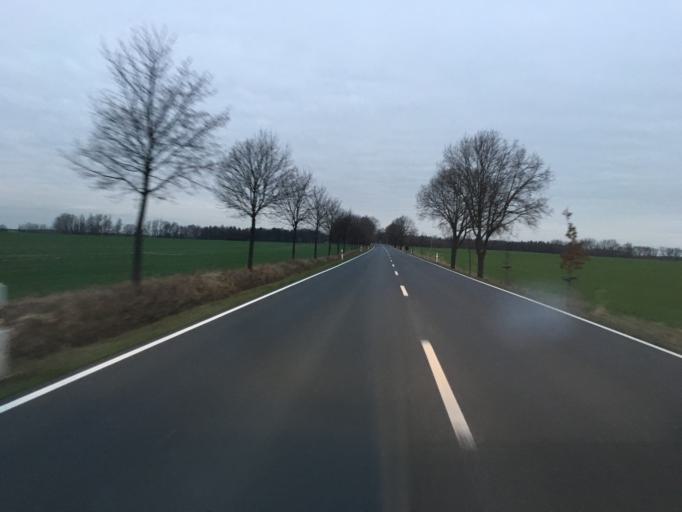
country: DE
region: Saxony
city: Oschatz
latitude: 51.3218
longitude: 13.0507
